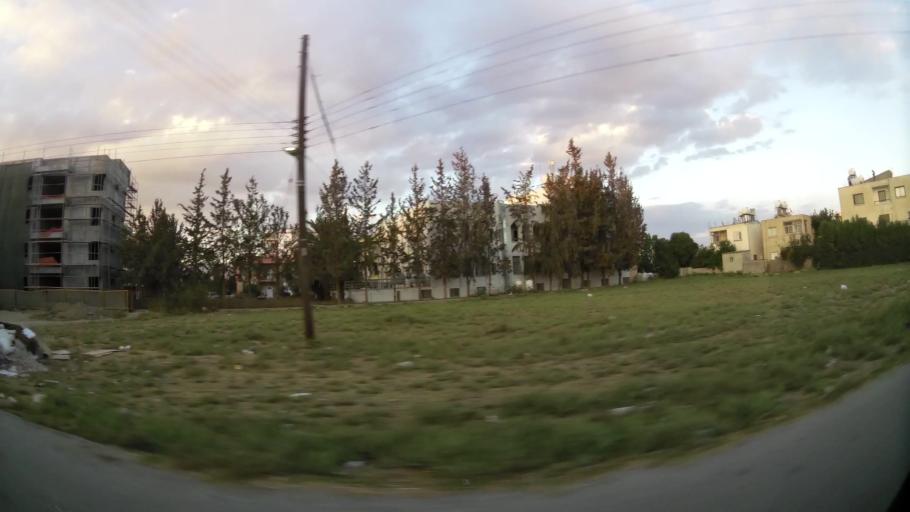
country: CY
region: Lefkosia
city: Nicosia
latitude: 35.1963
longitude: 33.3721
